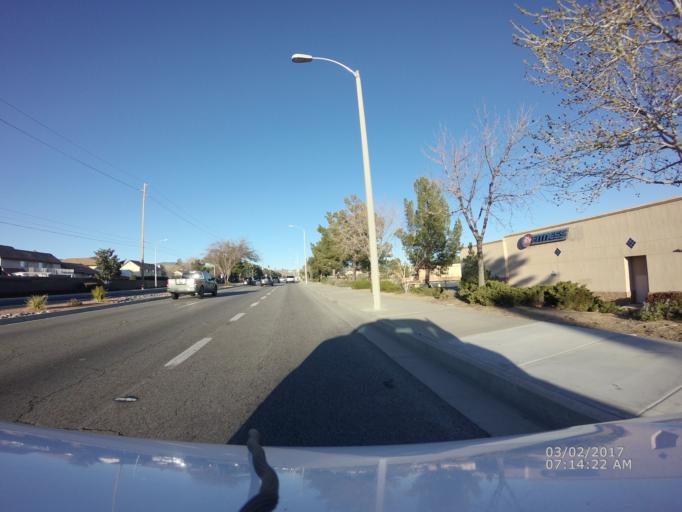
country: US
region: California
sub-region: Los Angeles County
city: Desert View Highlands
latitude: 34.6019
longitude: -118.1550
